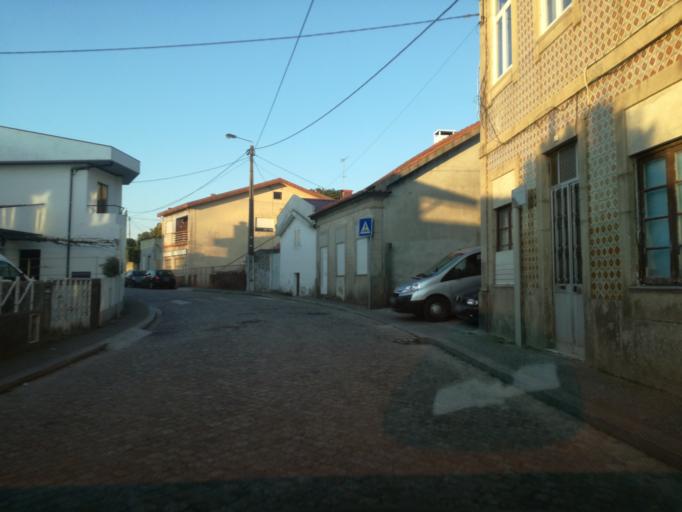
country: PT
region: Porto
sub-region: Maia
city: Milheiros
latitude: 41.2176
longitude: -8.5921
